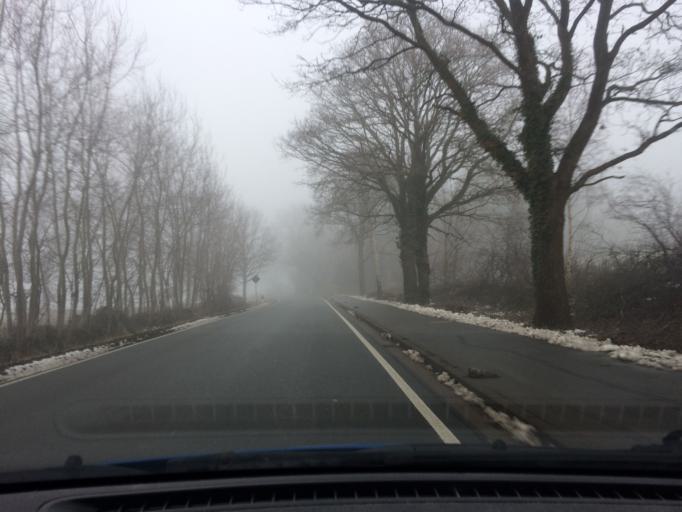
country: DE
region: Schleswig-Holstein
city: Kollow
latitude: 53.4786
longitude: 10.4645
